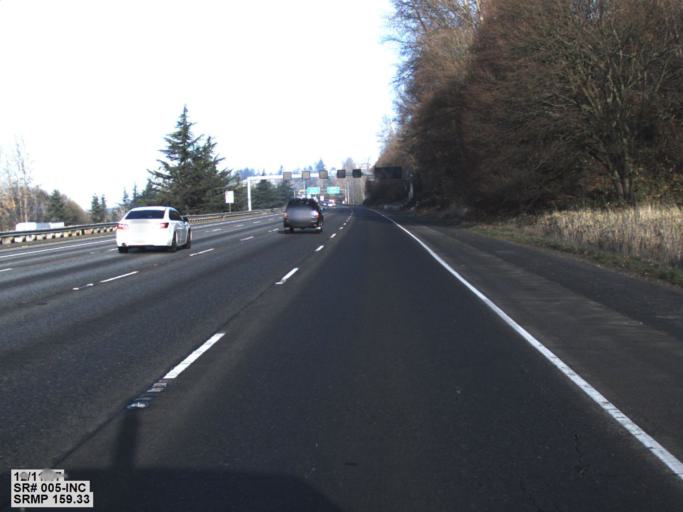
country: US
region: Washington
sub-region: King County
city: Riverton
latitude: 47.5255
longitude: -122.2917
